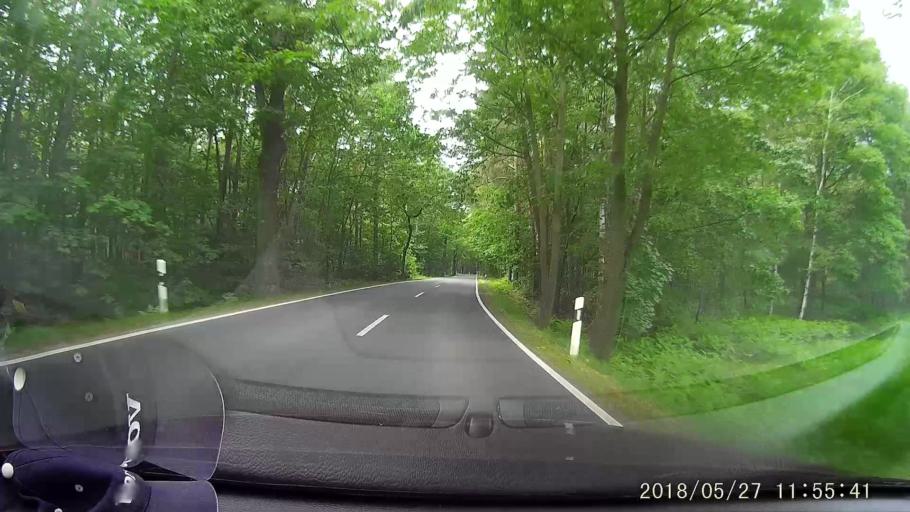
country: DE
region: Saxony
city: Quitzdorf
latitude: 51.3033
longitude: 14.7459
